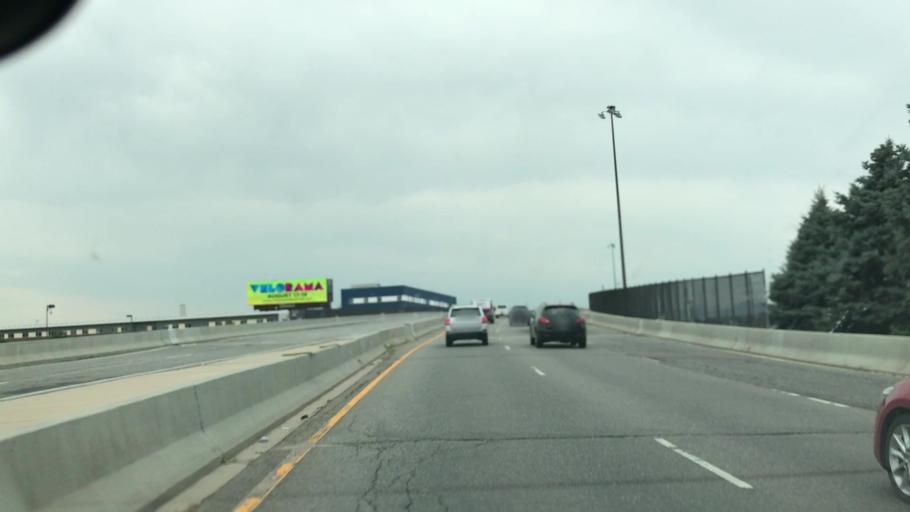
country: US
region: Colorado
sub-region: Denver County
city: Denver
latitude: 39.7442
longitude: -105.0107
